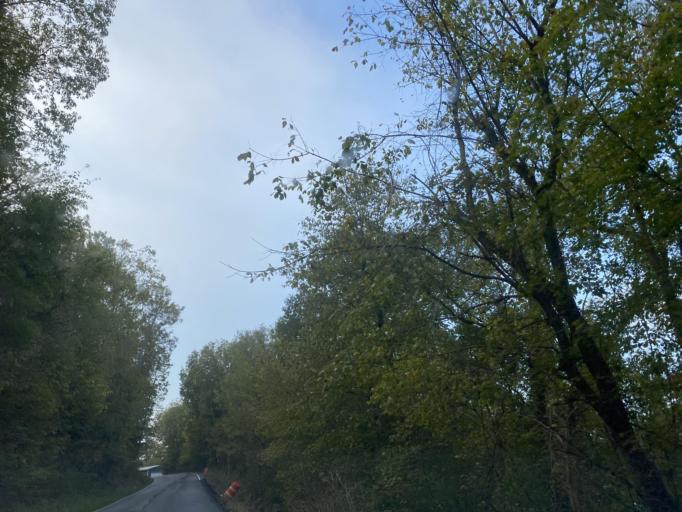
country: US
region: Kentucky
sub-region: Pendleton County
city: Falmouth
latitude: 38.7420
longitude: -84.3165
